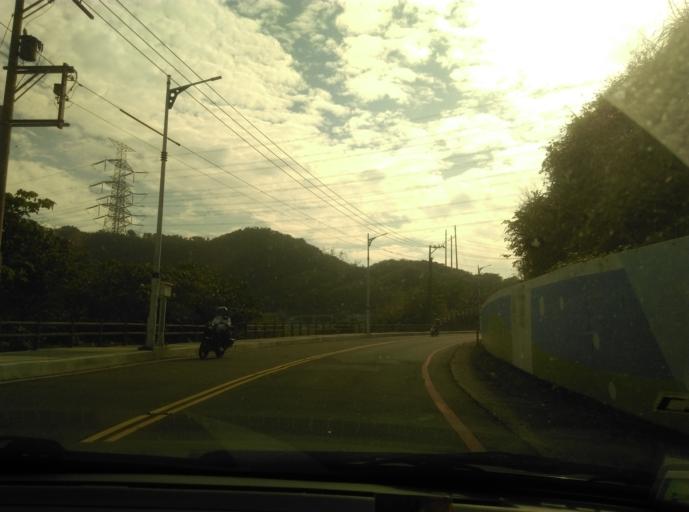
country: TW
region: Taiwan
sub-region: Keelung
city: Keelung
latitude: 25.1589
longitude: 121.7324
